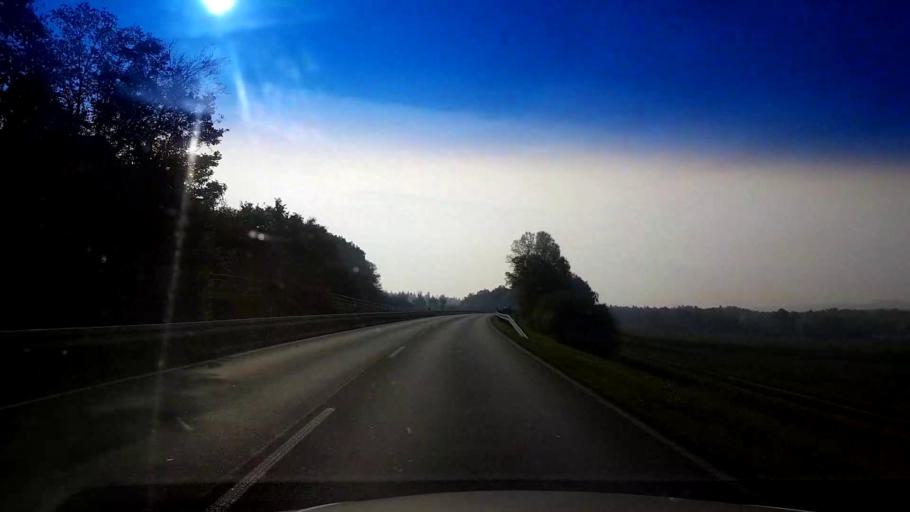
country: DE
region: Bavaria
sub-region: Upper Franconia
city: Neuenmarkt
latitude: 50.0969
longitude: 11.6067
